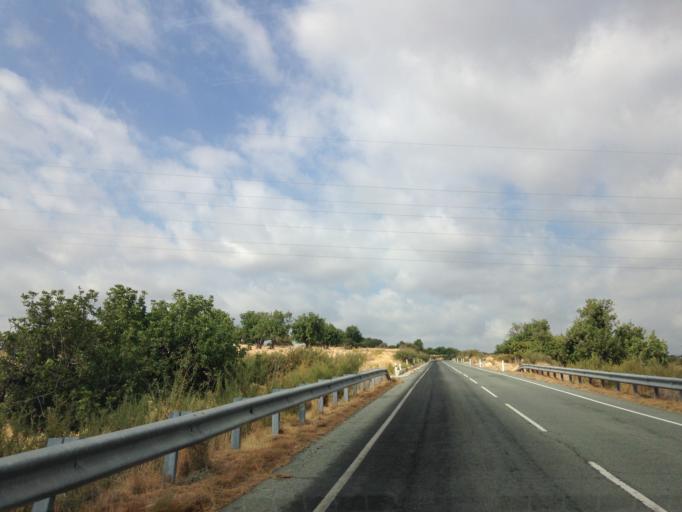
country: CY
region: Limassol
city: Pissouri
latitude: 34.7073
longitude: 32.7660
